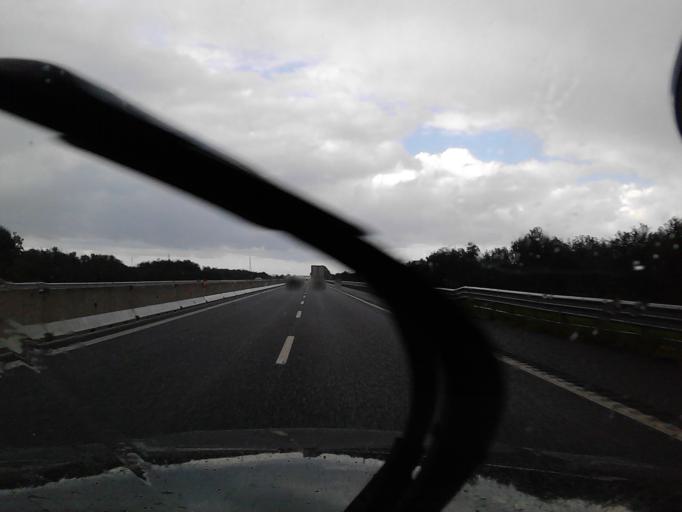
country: IT
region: Apulia
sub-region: Provincia di Bari
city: Giovinazzo
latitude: 41.1607
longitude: 16.6321
